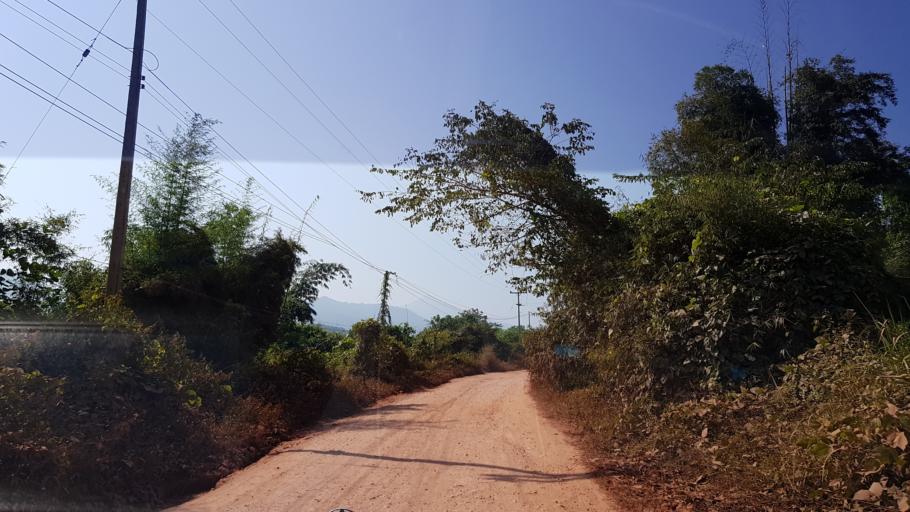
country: LA
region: Oudomxai
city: Muang Xay
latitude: 20.7138
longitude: 102.0377
